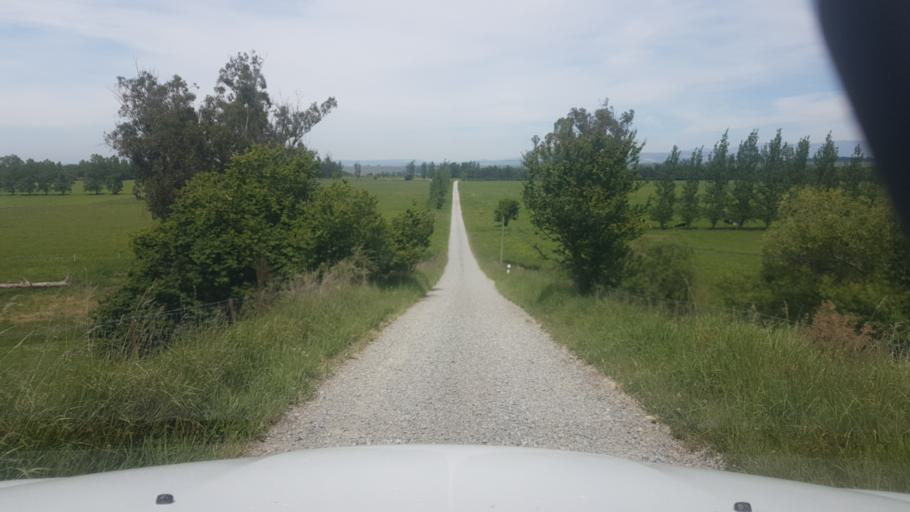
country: NZ
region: Canterbury
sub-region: Timaru District
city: Pleasant Point
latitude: -44.1964
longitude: 171.0911
